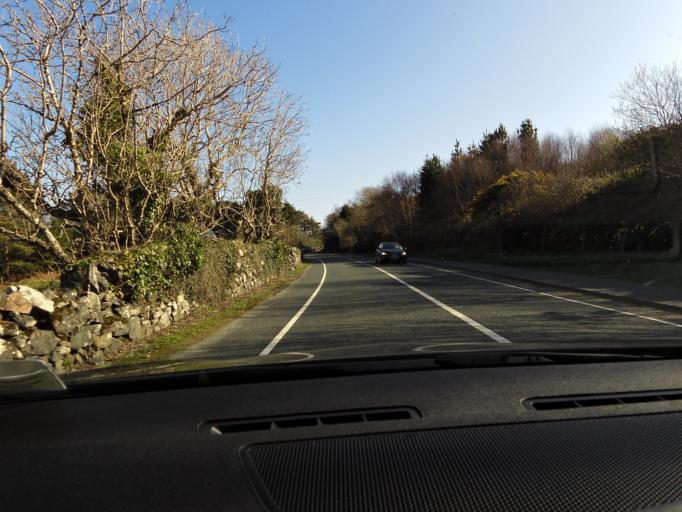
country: IE
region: Connaught
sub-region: County Galway
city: Clifden
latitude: 53.4808
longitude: -10.0214
